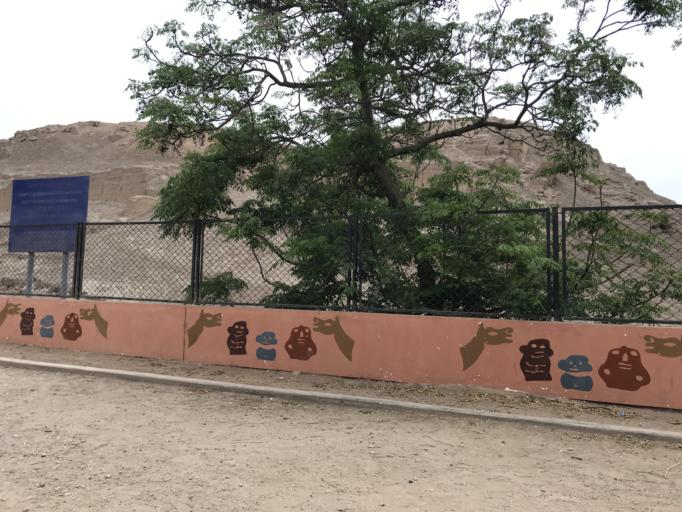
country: PE
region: Callao
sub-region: Callao
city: Callao
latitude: -12.0718
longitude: -77.0844
